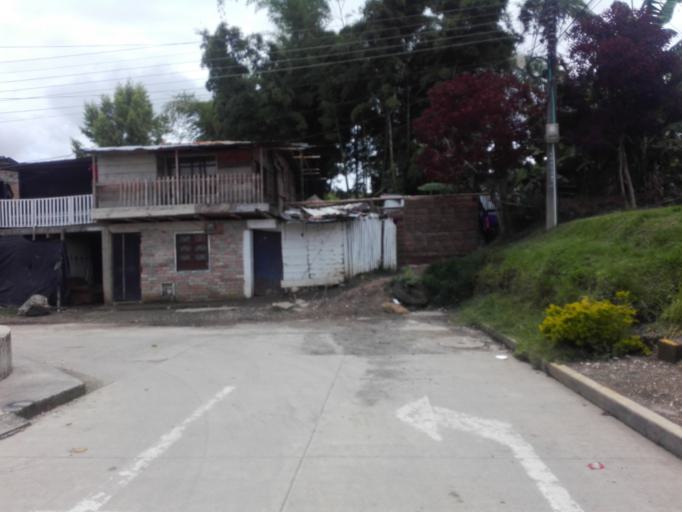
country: CO
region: Cauca
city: Popayan
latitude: 2.3526
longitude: -76.6773
